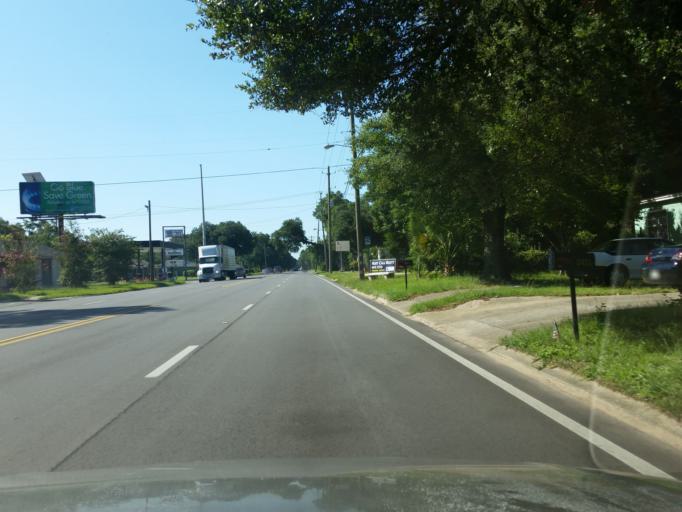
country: US
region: Florida
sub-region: Escambia County
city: Goulding
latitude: 30.4451
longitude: -87.2122
